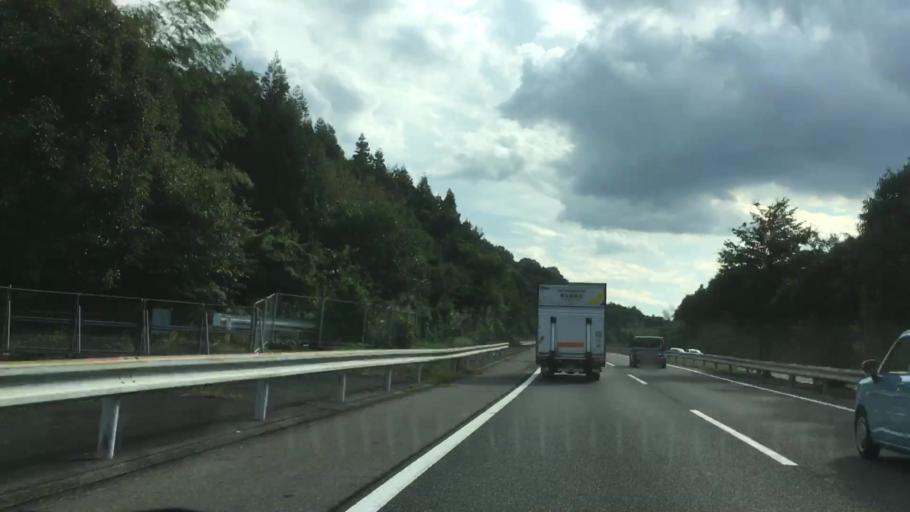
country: JP
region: Yamaguchi
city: Iwakuni
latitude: 34.1466
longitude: 132.1257
